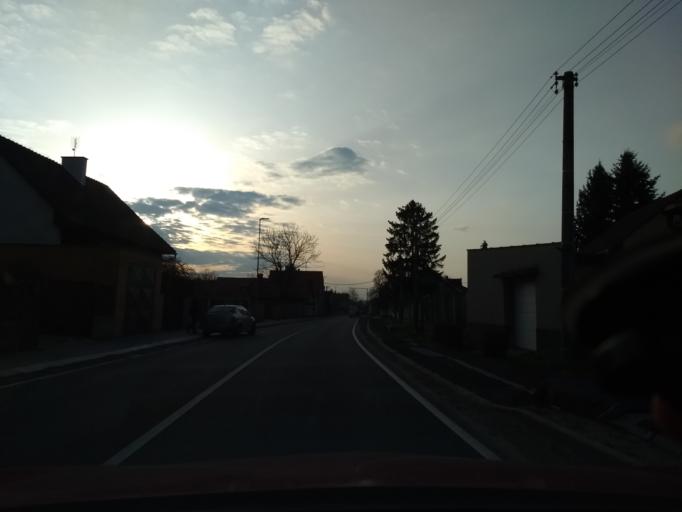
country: CZ
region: Central Bohemia
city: Jenec
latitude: 50.0521
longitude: 14.1739
